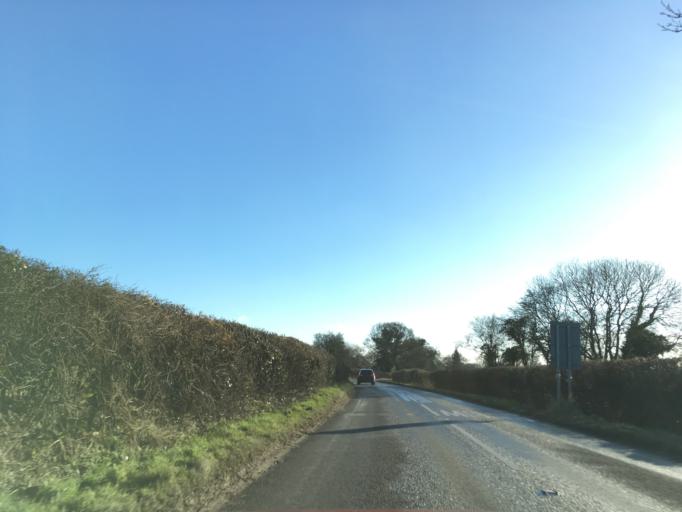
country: GB
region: England
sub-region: Wiltshire
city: Biddestone
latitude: 51.4762
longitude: -2.1762
